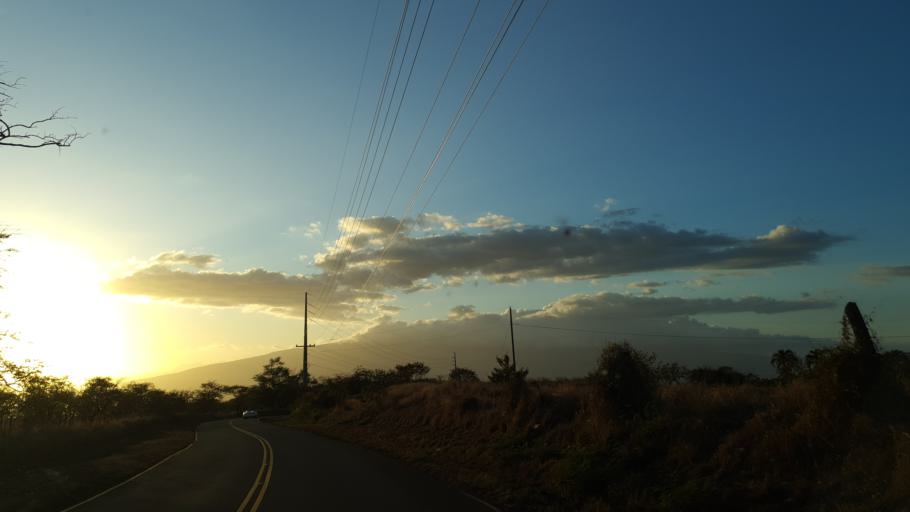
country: US
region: Hawaii
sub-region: Maui County
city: Pukalani
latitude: 20.7944
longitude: -156.3648
